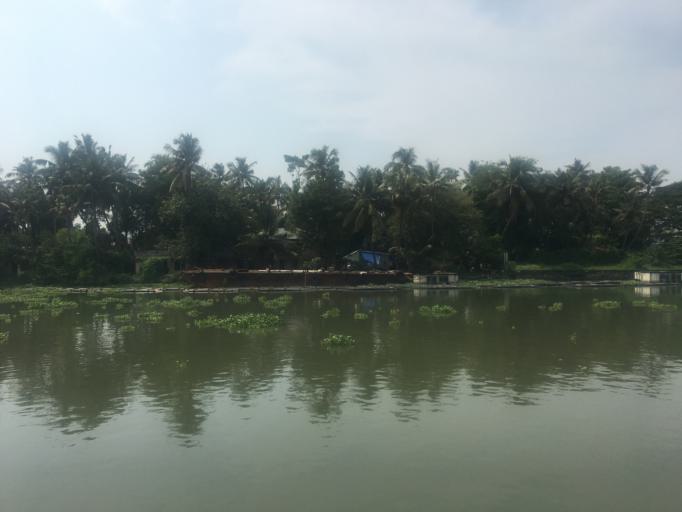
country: IN
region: Kerala
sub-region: Ernakulam
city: Cochin
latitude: 9.9904
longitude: 76.2674
